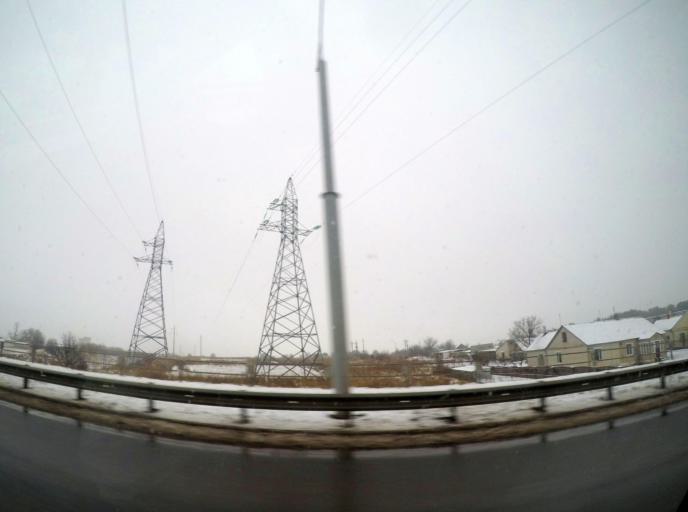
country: BY
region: Grodnenskaya
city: Hrodna
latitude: 53.6350
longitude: 23.8100
